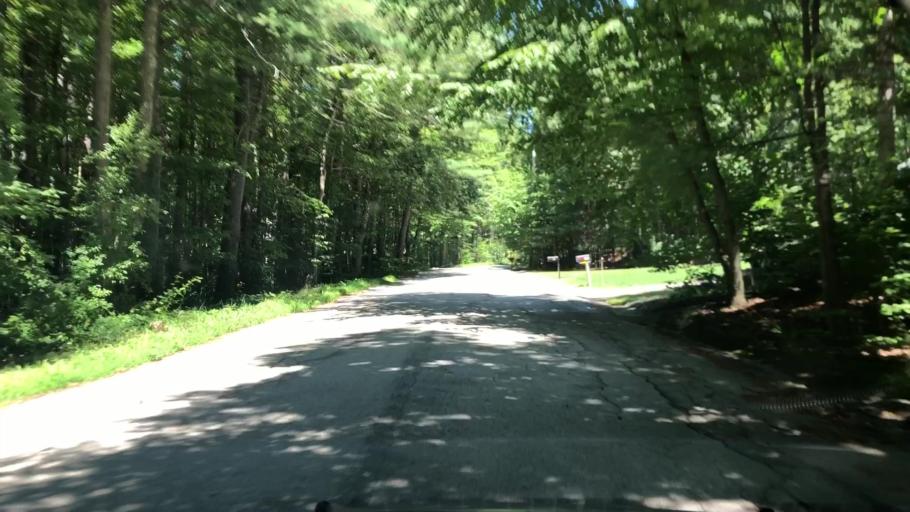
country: US
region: New Hampshire
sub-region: Hillsborough County
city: Milford
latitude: 42.8337
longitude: -71.5862
